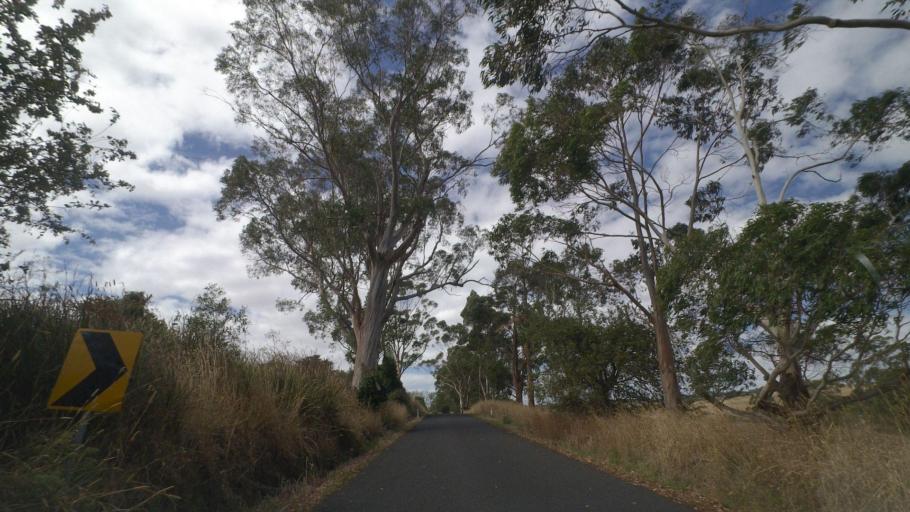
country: AU
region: Victoria
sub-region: Bass Coast
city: North Wonthaggi
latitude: -38.4035
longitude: 145.7631
